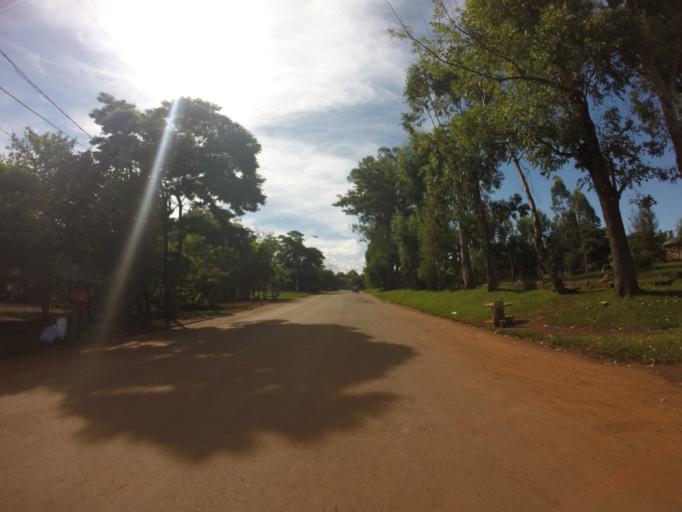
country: PY
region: Alto Parana
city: Ciudad del Este
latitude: -25.3996
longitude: -54.6515
